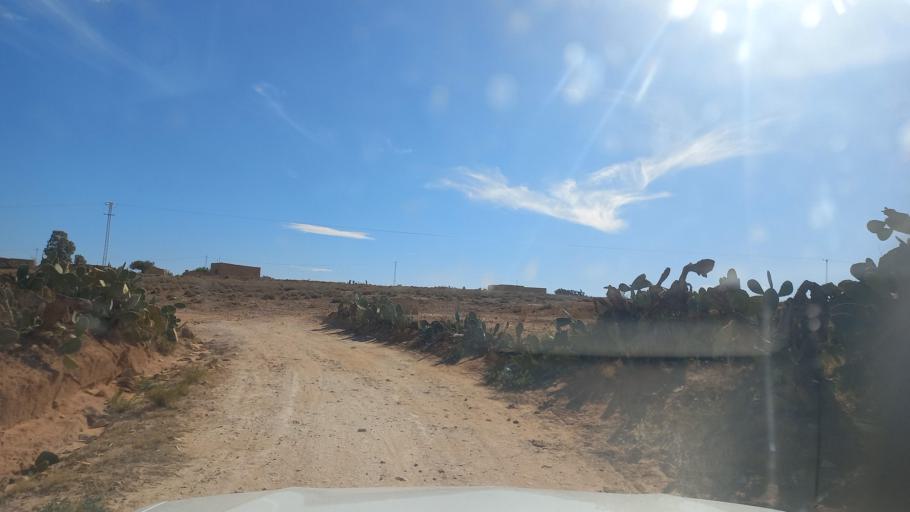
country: TN
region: Al Qasrayn
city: Kasserine
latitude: 35.2077
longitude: 8.9735
